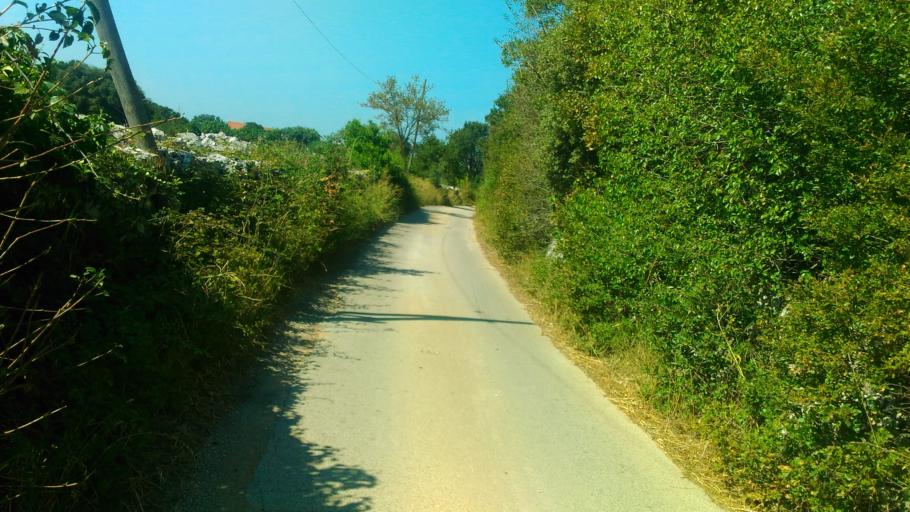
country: IT
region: Apulia
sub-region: Provincia di Bari
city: Noci
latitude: 40.8096
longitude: 17.1811
